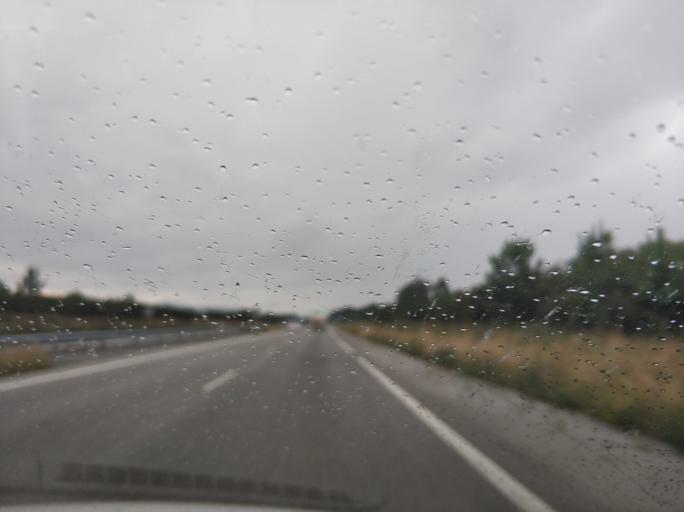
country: ES
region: Asturias
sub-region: Province of Asturias
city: Tapia de Casariego
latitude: 43.5424
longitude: -6.9536
